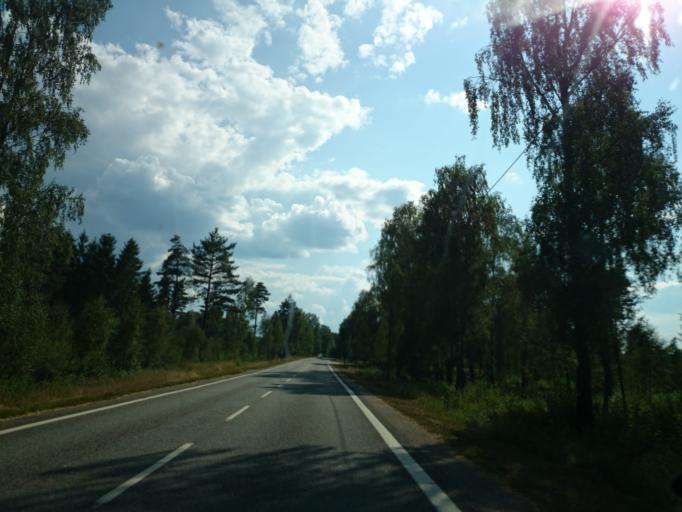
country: SE
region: Joenkoeping
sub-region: Varnamo Kommun
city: Forsheda
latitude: 57.0631
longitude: 13.8513
